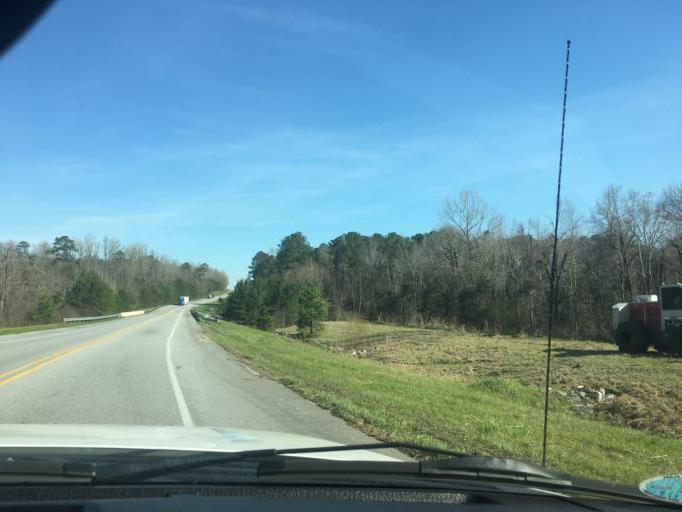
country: US
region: Alabama
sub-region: Lee County
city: Auburn
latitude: 32.4327
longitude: -85.4689
